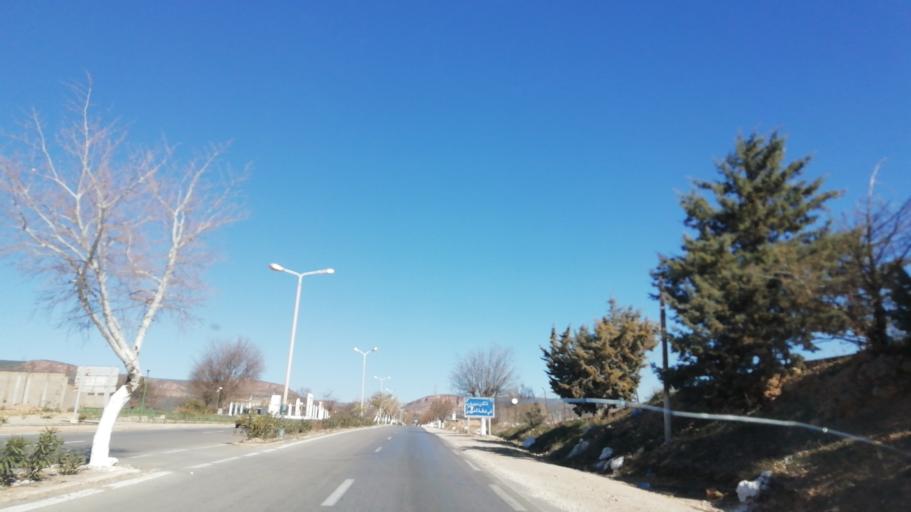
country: DZ
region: Tlemcen
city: Sebdou
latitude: 34.6584
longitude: -1.3241
